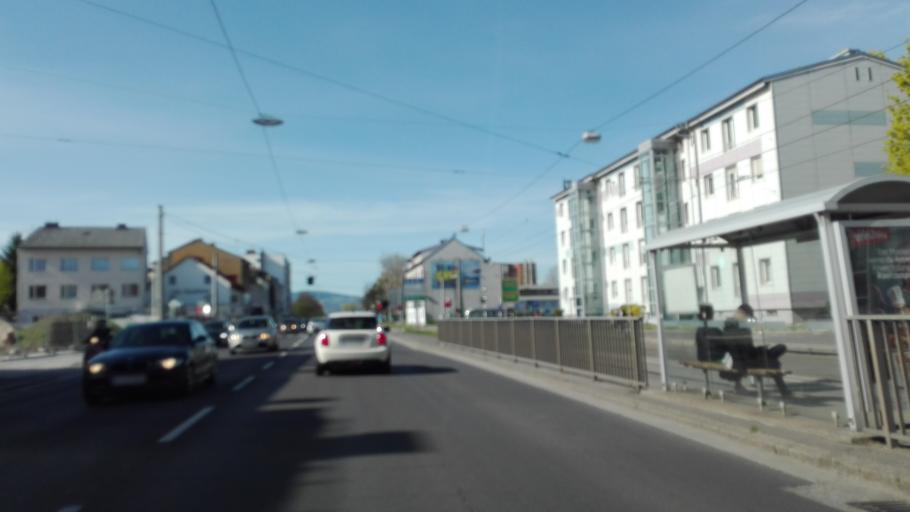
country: AT
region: Upper Austria
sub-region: Politischer Bezirk Urfahr-Umgebung
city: Steyregg
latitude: 48.2558
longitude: 14.3224
